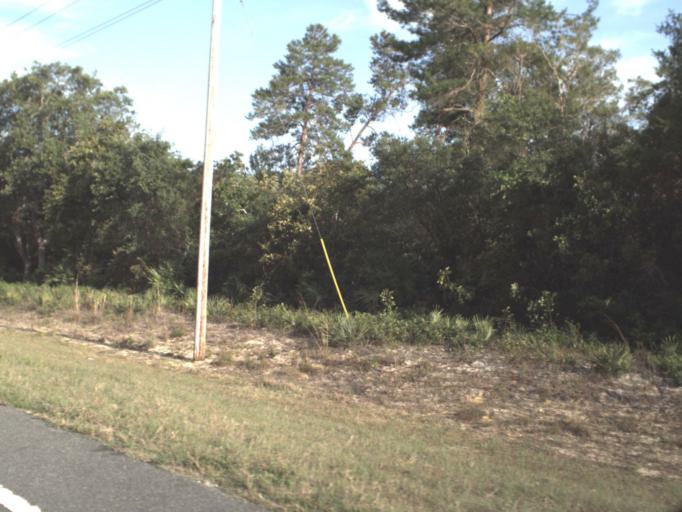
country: US
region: Florida
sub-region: Lake County
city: Astor
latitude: 29.1589
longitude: -81.5979
